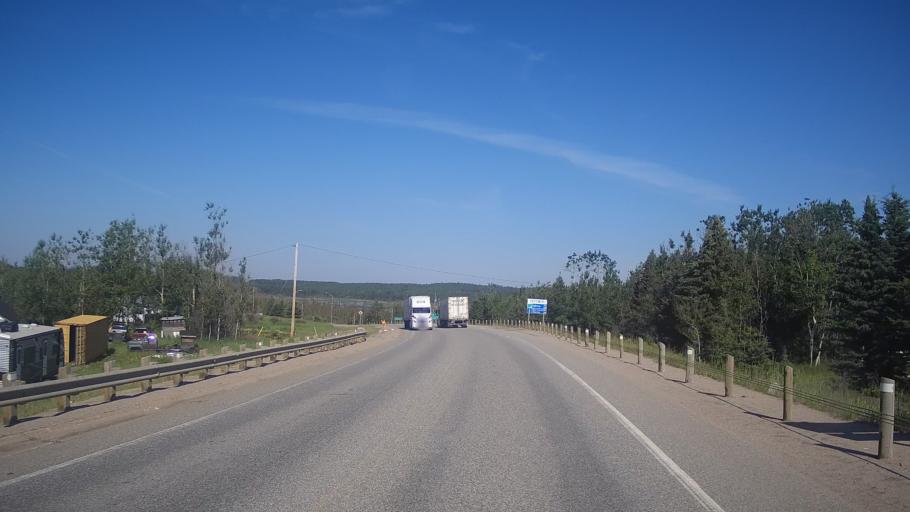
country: CA
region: Ontario
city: Dryden
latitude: 49.6908
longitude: -92.4995
